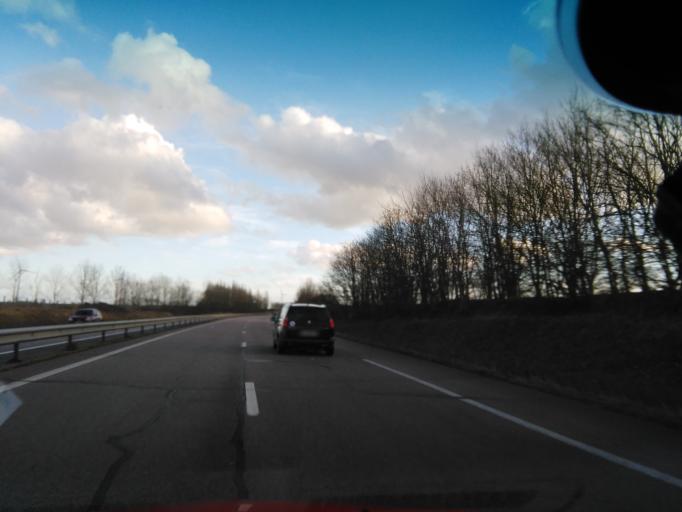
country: FR
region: Lower Normandy
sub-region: Departement du Calvados
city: Potigny
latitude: 48.9440
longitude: -0.2131
